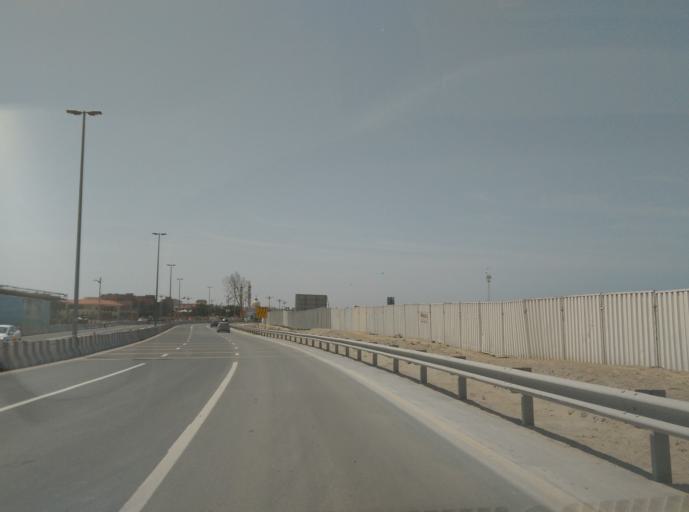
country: AE
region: Dubai
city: Dubai
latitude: 25.1964
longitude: 55.2351
